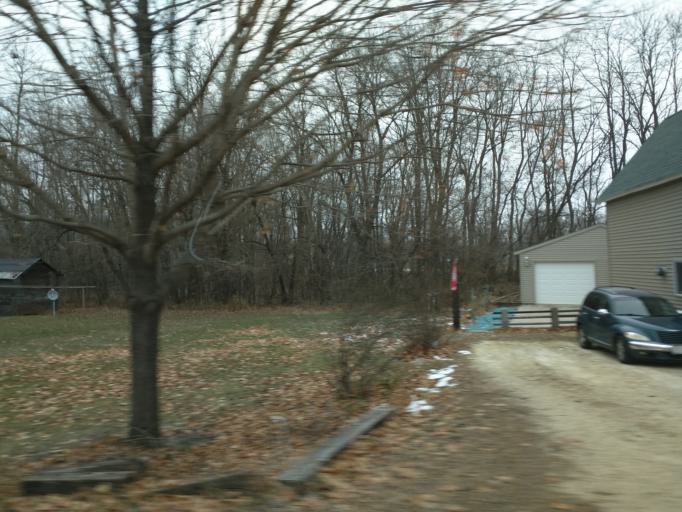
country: US
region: Wisconsin
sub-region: La Crosse County
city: French Island
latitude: 43.8477
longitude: -91.2660
